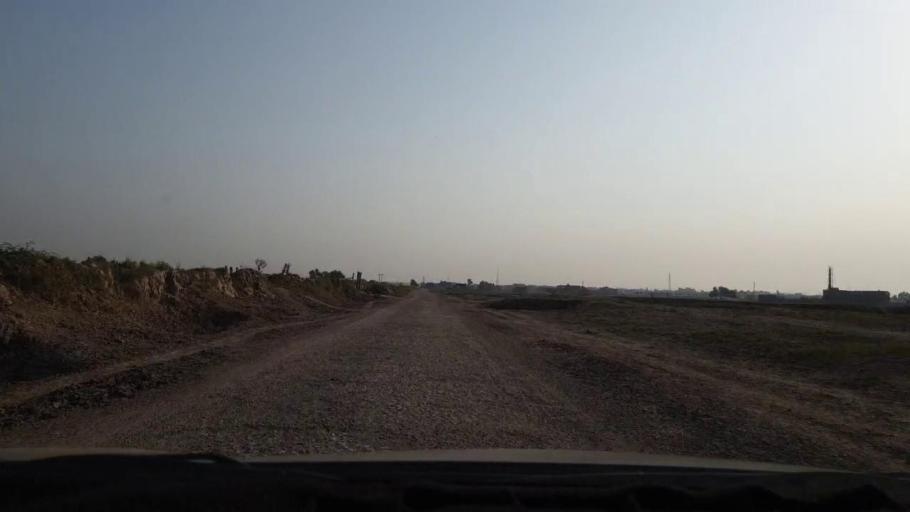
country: PK
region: Sindh
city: Larkana
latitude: 27.5231
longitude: 68.1936
